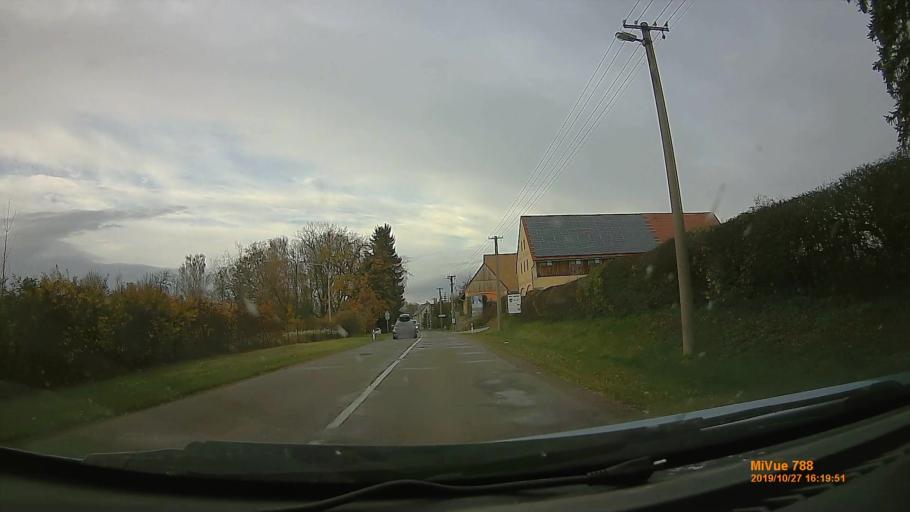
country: CZ
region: Kralovehradecky
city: Broumov
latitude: 50.5758
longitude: 16.3428
